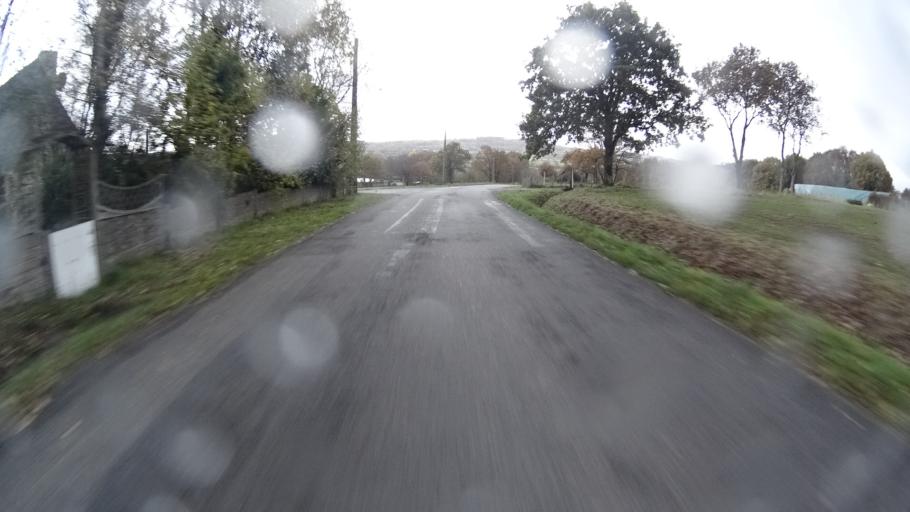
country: FR
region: Brittany
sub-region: Departement d'Ille-et-Vilaine
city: Sainte-Marie
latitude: 47.6751
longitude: -2.0351
